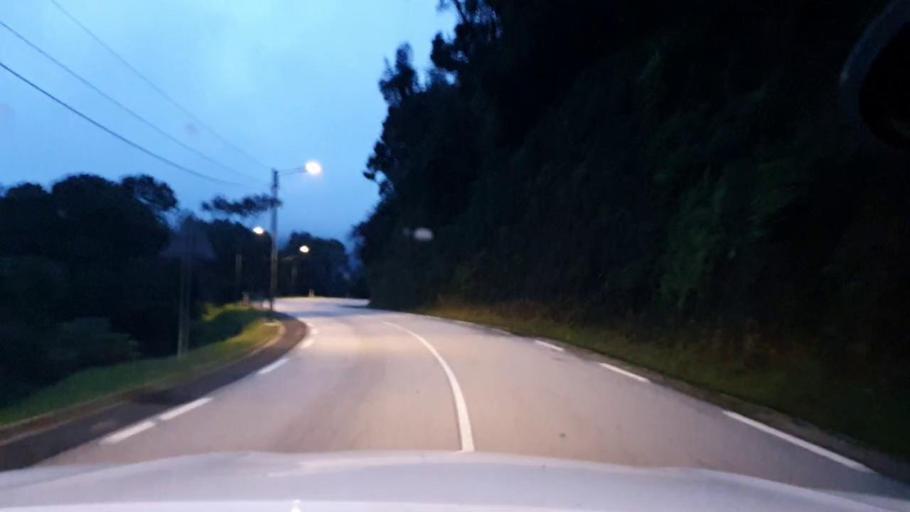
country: RW
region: Southern Province
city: Nzega
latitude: -2.5308
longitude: 29.3810
